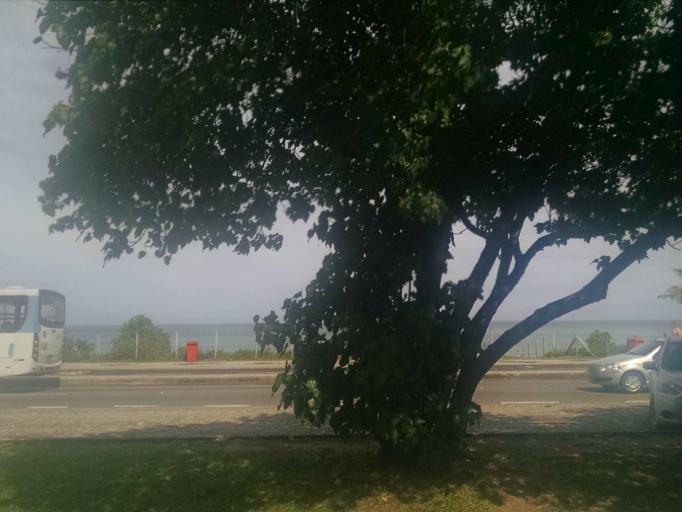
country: BR
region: Rio de Janeiro
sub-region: Rio De Janeiro
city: Rio de Janeiro
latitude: -23.0116
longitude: -43.3239
